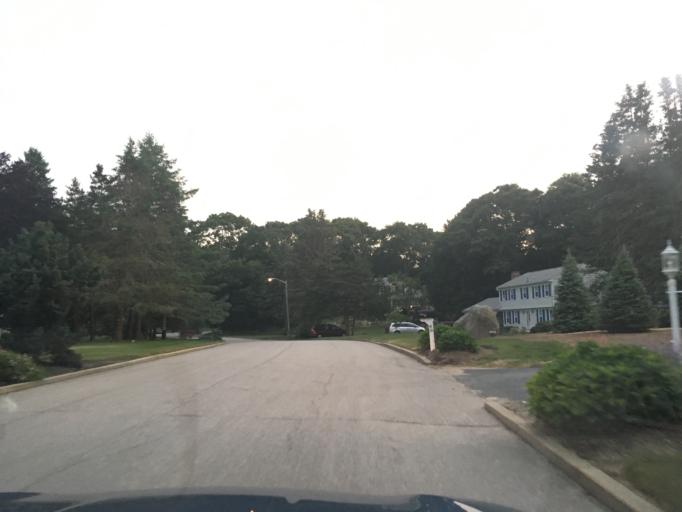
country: US
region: Rhode Island
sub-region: Washington County
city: Exeter
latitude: 41.6276
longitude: -71.5204
